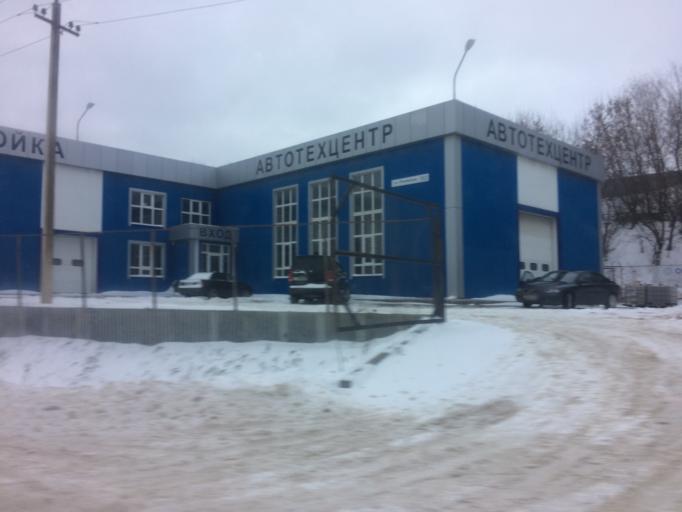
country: RU
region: Tula
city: Tula
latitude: 54.1693
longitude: 37.6349
